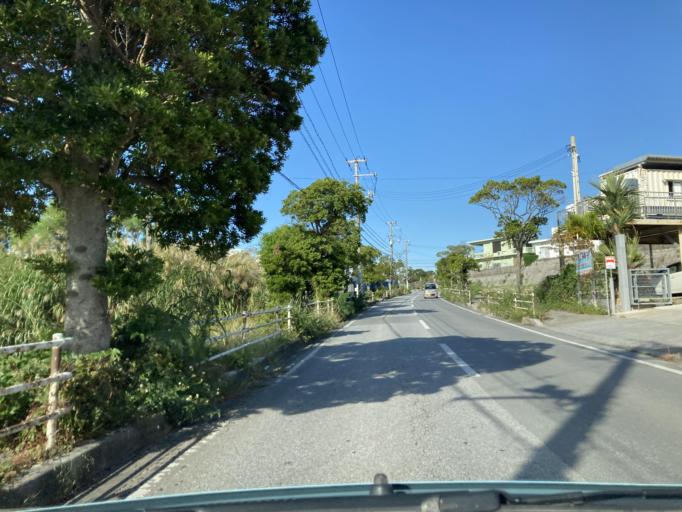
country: JP
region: Okinawa
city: Tomigusuku
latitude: 26.1764
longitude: 127.7057
